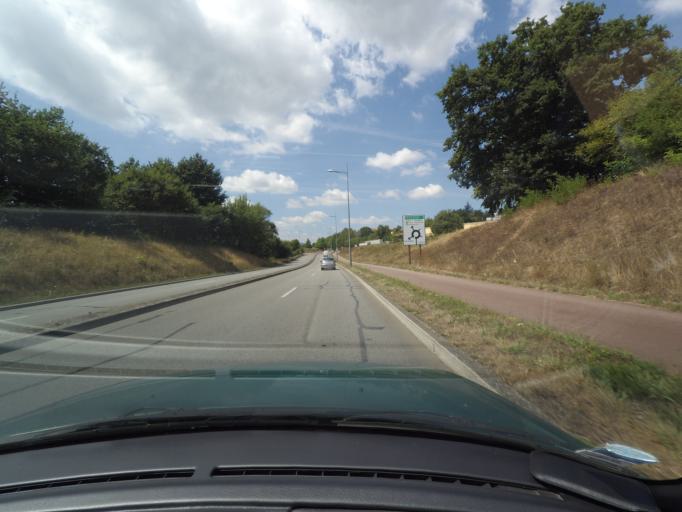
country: FR
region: Limousin
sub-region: Departement de la Haute-Vienne
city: Limoges
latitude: 45.8075
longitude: 1.2667
